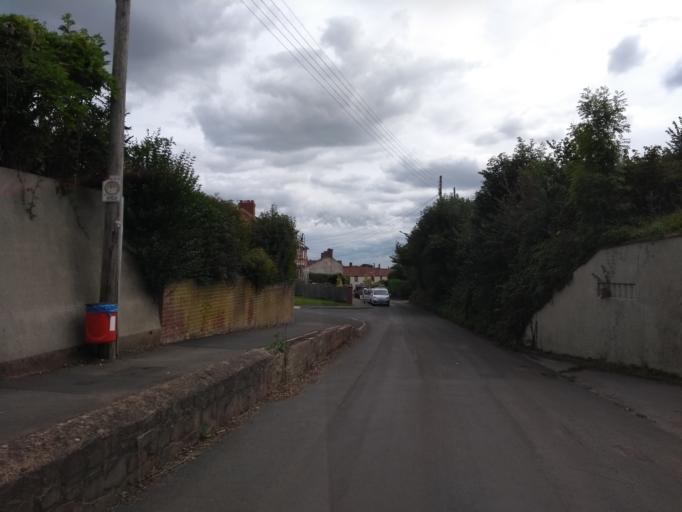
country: GB
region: England
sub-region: Somerset
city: North Petherton
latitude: 51.0905
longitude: -3.0216
